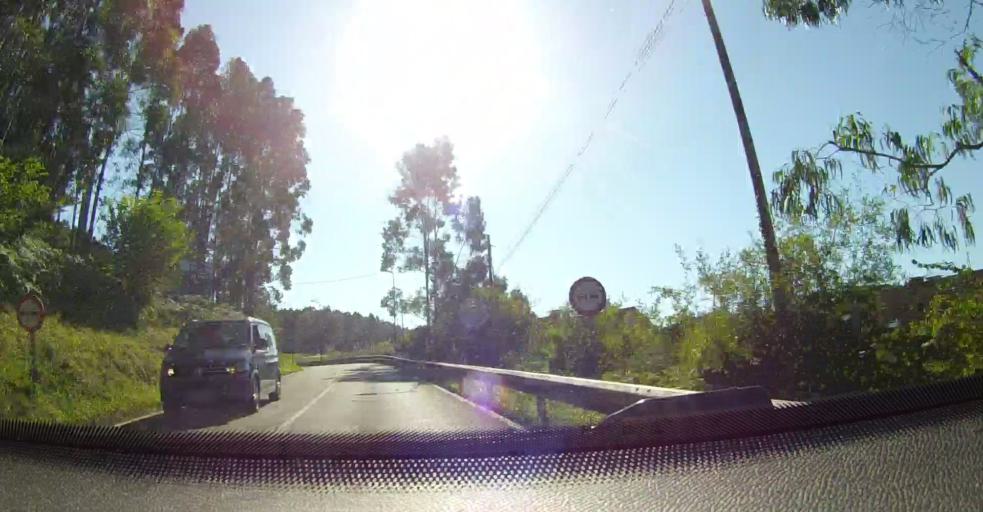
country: ES
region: Asturias
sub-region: Province of Asturias
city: Ribadesella
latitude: 43.4658
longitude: -5.0863
